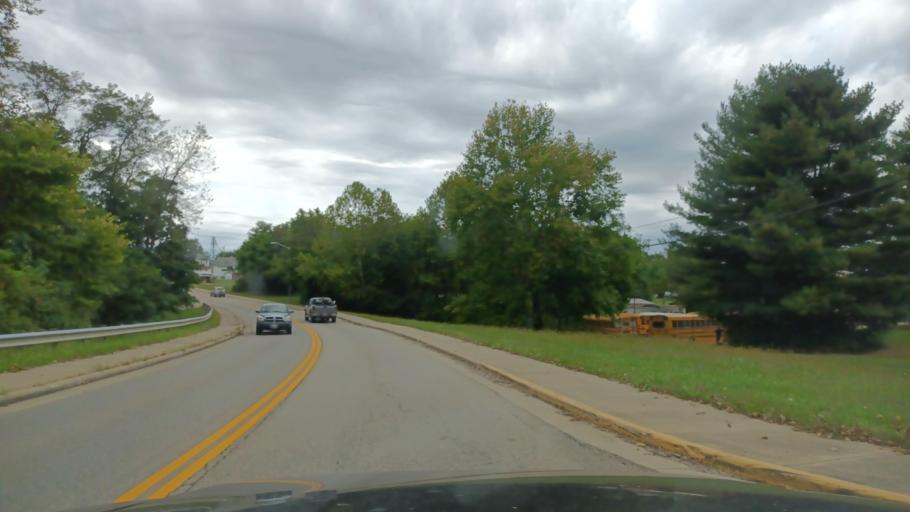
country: US
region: Ohio
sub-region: Vinton County
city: McArthur
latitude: 39.2461
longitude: -82.4743
